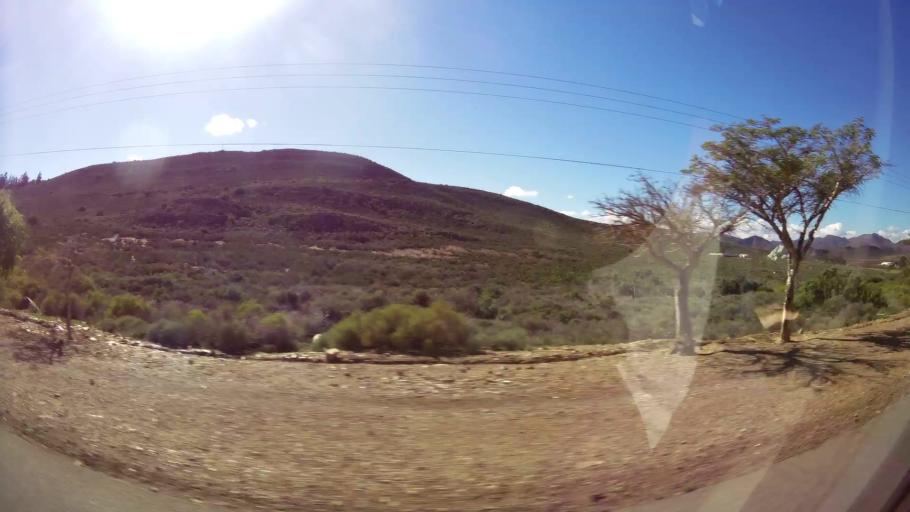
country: ZA
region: Western Cape
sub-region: Cape Winelands District Municipality
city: Ashton
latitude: -33.7677
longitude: 20.1285
